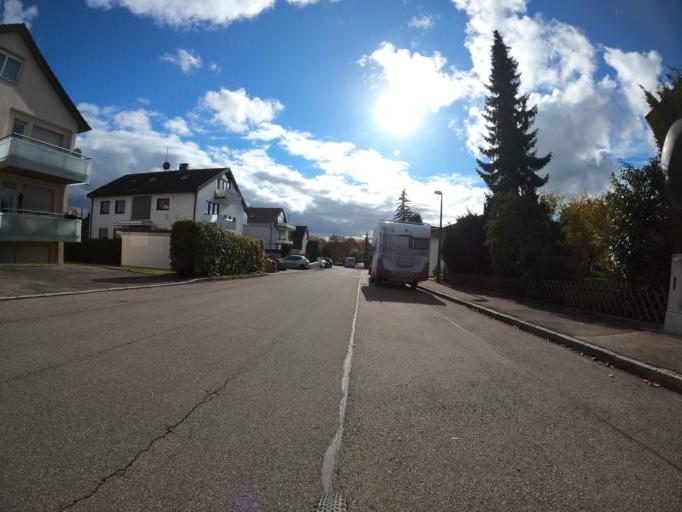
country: DE
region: Baden-Wuerttemberg
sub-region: Regierungsbezirk Stuttgart
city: Magstadt
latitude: 48.7212
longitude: 8.9617
